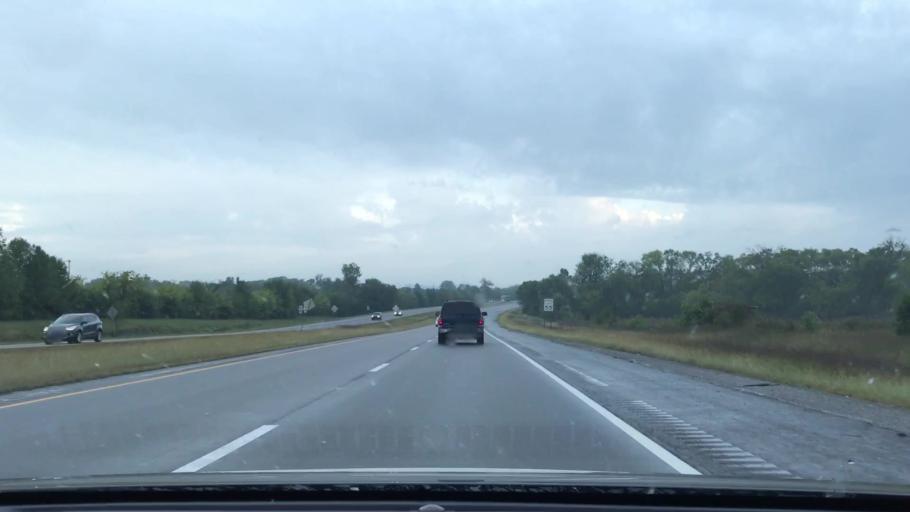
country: US
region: Tennessee
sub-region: Sumner County
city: Gallatin
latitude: 36.3995
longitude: -86.4790
